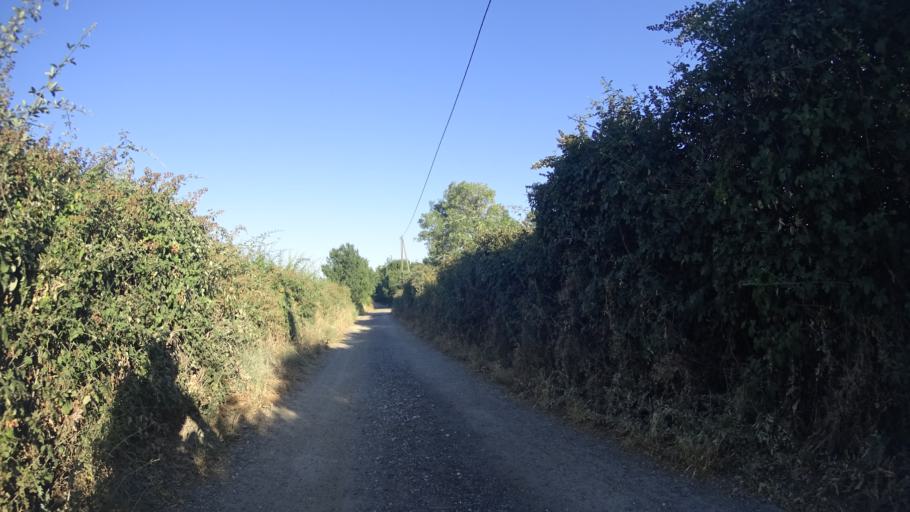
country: ES
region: Madrid
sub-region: Provincia de Madrid
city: Galapagar
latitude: 40.5666
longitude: -3.9933
